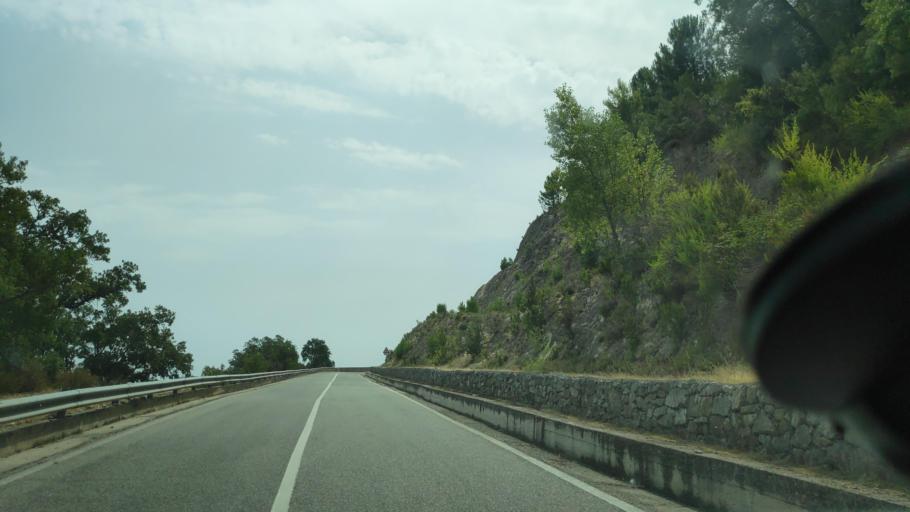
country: IT
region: Calabria
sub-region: Provincia di Catanzaro
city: San Sostene
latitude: 38.6382
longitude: 16.5101
